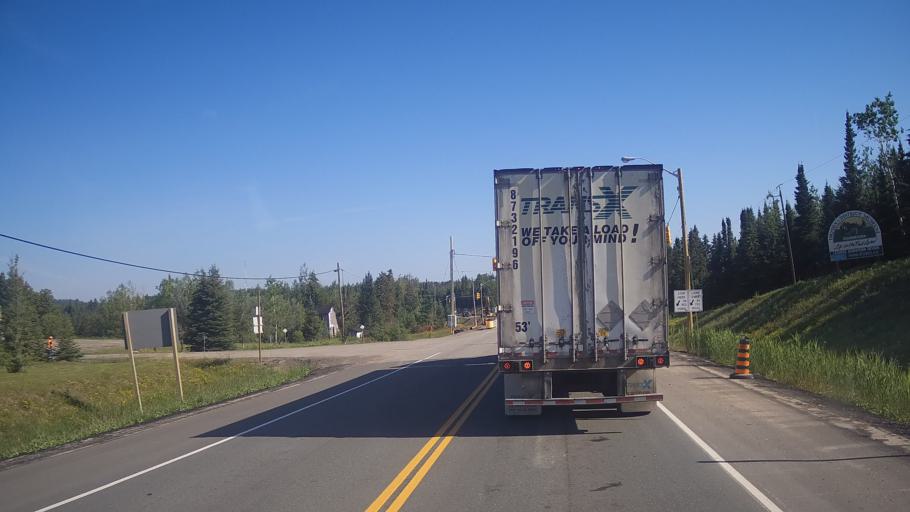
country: CA
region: Ontario
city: Dryden
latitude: 49.6835
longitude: -92.4927
